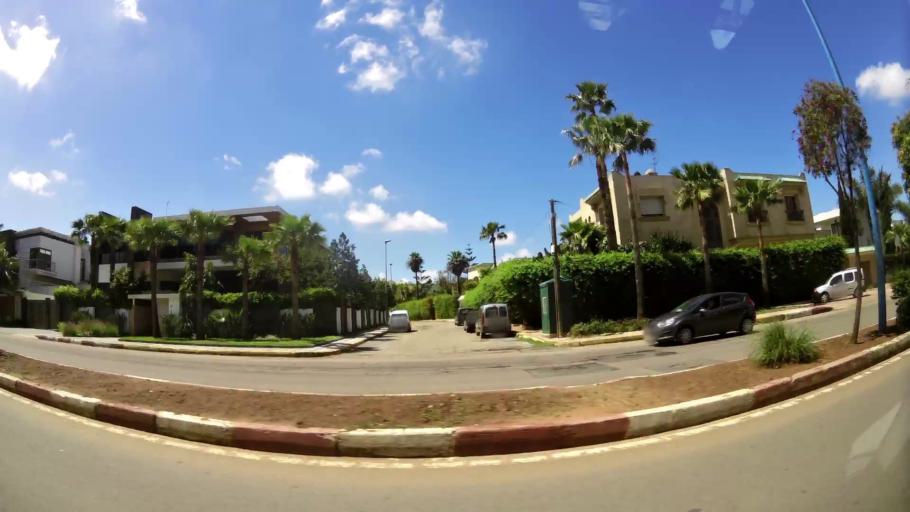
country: MA
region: Grand Casablanca
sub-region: Casablanca
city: Casablanca
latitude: 33.5284
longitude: -7.6307
